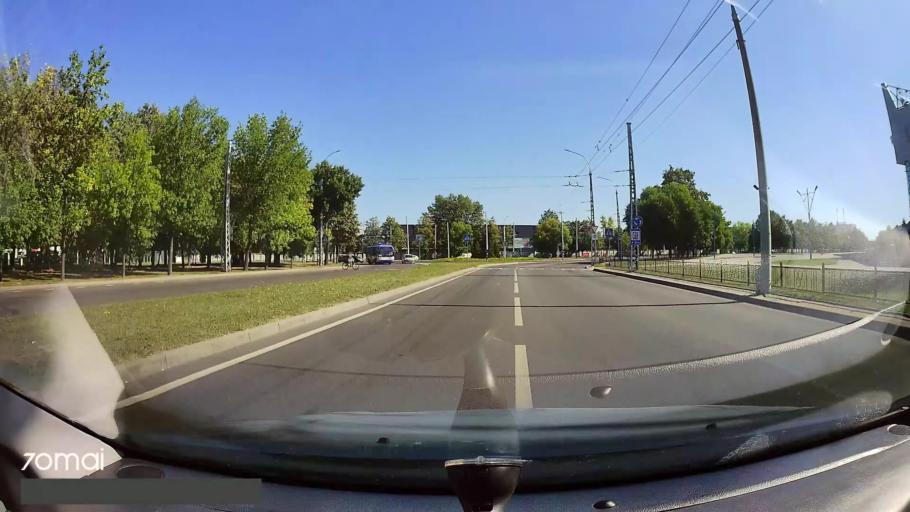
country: BY
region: Brest
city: Brest
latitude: 52.1148
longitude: 23.7774
